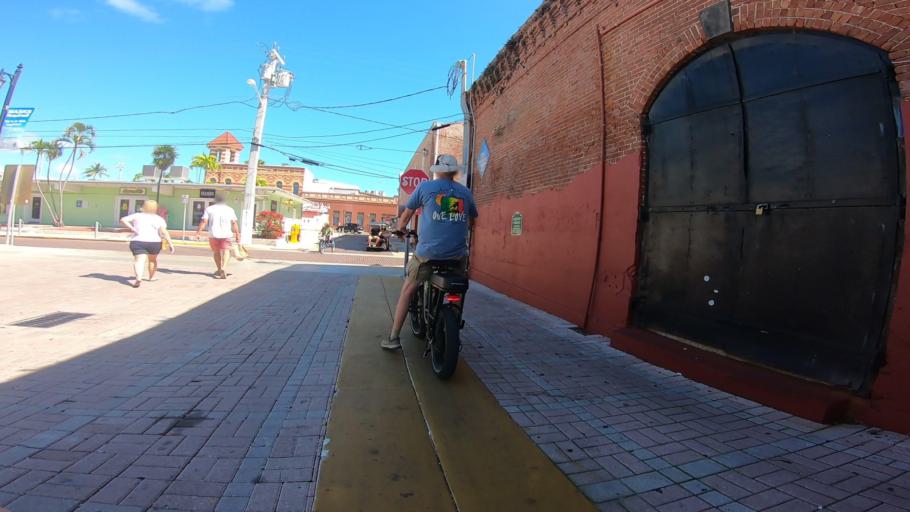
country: US
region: Florida
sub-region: Monroe County
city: Key West
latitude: 24.5601
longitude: -81.8068
